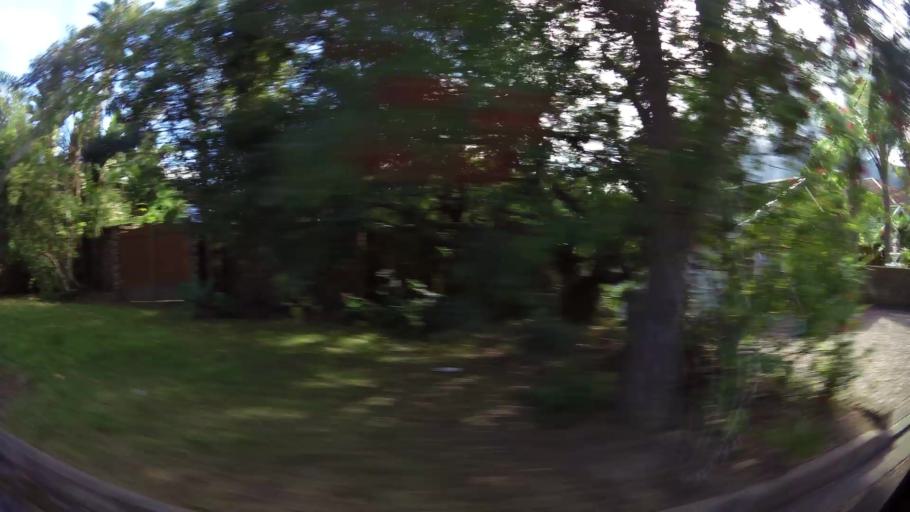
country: ZA
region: Western Cape
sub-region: Eden District Municipality
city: George
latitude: -33.9587
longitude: 22.4923
